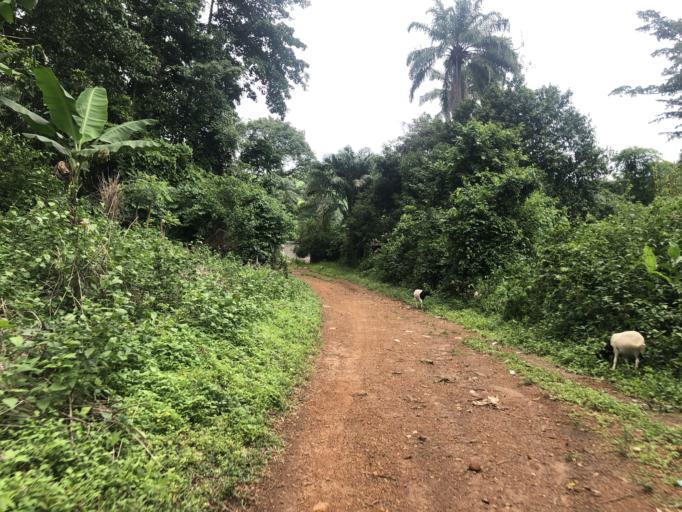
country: SL
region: Northern Province
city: Bumbuna
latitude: 8.9929
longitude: -11.7539
